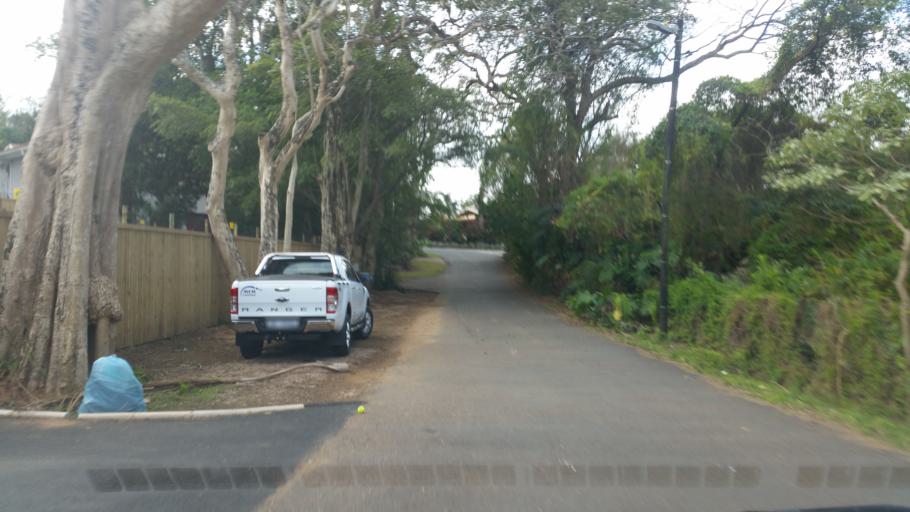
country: ZA
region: KwaZulu-Natal
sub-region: eThekwini Metropolitan Municipality
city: Berea
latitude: -29.8315
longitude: 30.9253
